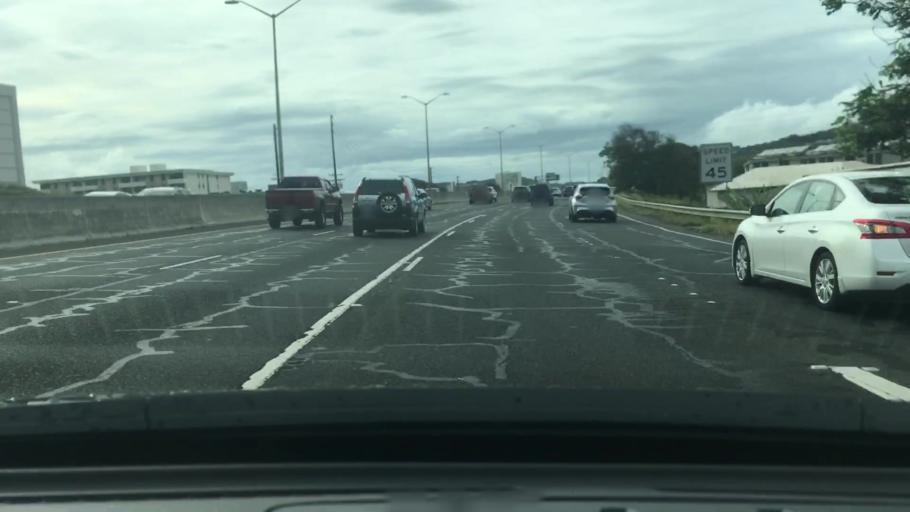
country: US
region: Hawaii
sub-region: Honolulu County
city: Honolulu
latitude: 21.2914
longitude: -157.8183
